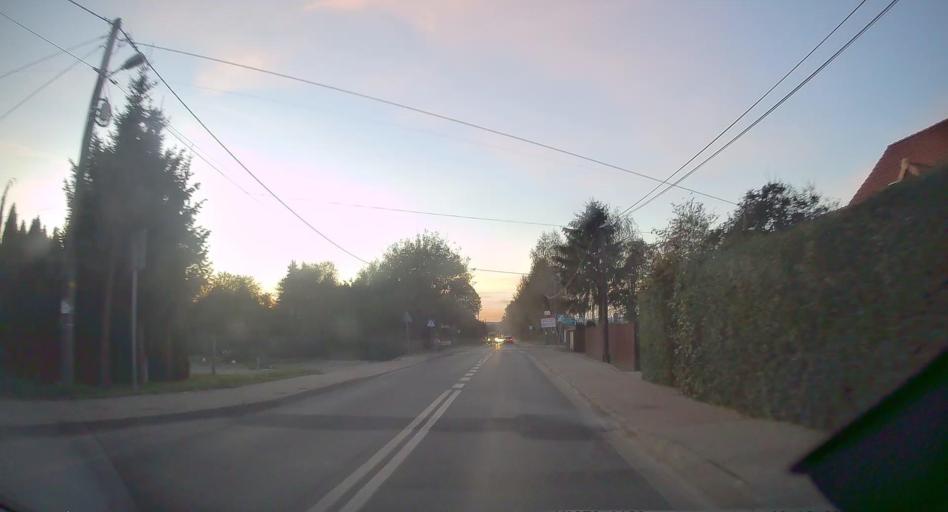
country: PL
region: Lesser Poland Voivodeship
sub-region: Powiat krakowski
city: Zabierzow
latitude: 50.1223
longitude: 19.8216
